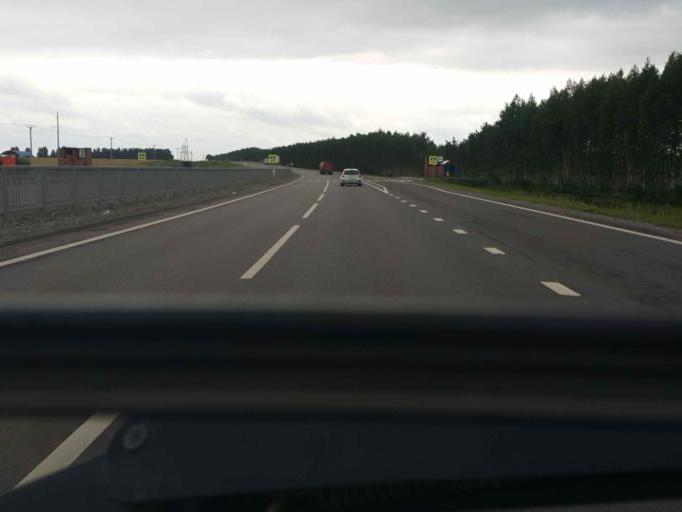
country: RU
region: Tambov
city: Zavoronezhskoye
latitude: 52.8763
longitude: 40.7501
